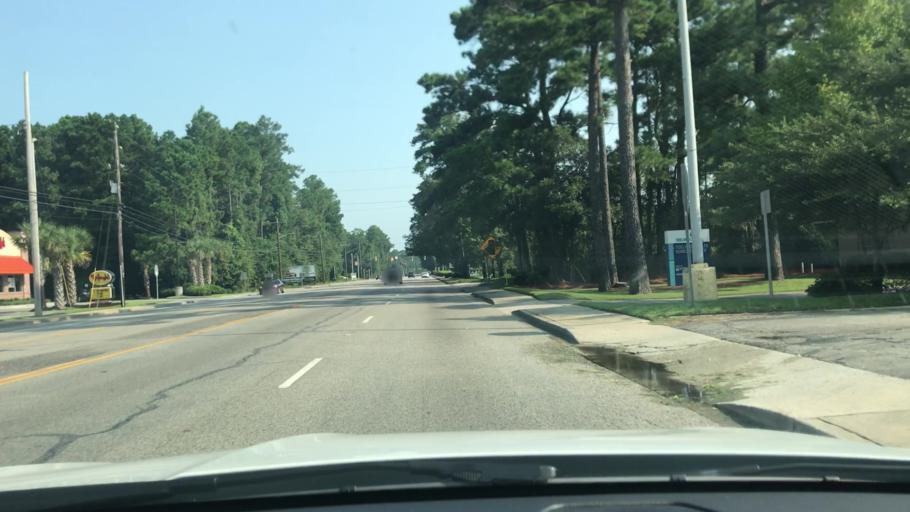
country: US
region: South Carolina
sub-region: Georgetown County
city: Georgetown
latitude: 33.3920
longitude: -79.2890
